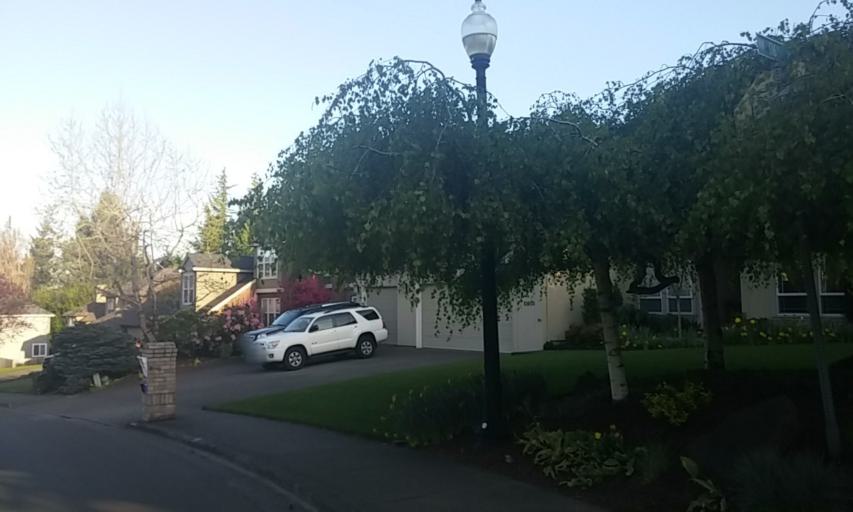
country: US
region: Oregon
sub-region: Washington County
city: Cedar Mill
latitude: 45.5422
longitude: -122.7965
